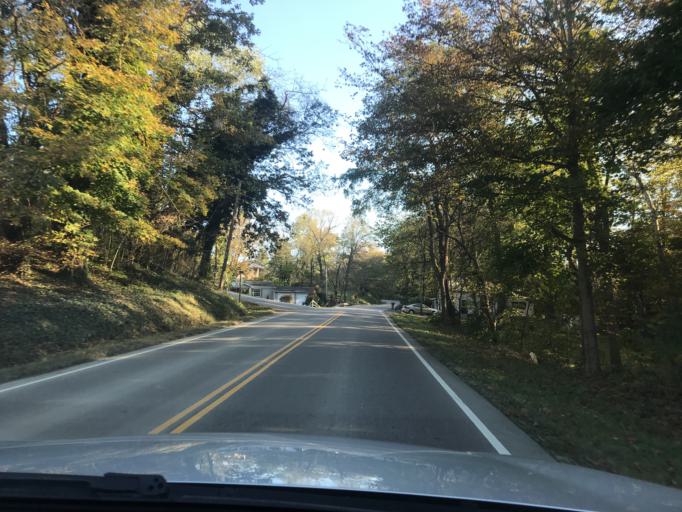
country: US
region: Ohio
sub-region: Pike County
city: Waverly
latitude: 39.0895
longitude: -82.9663
